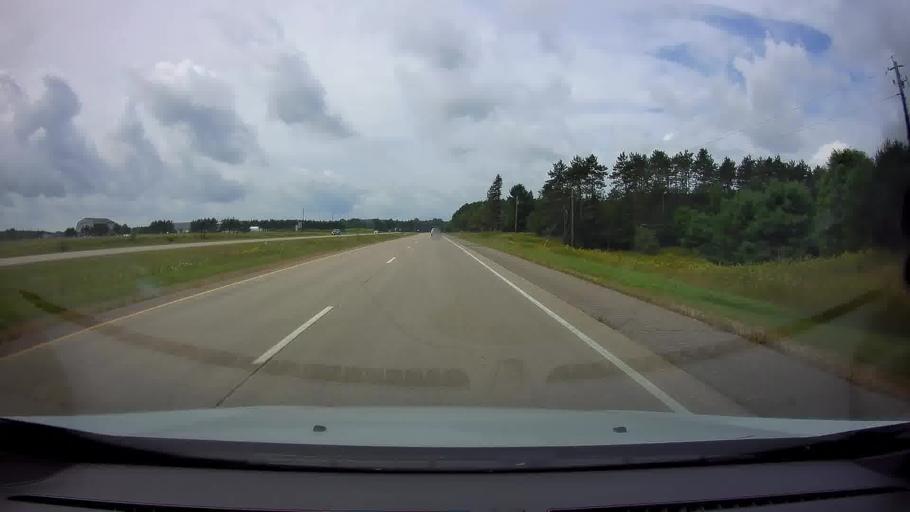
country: US
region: Wisconsin
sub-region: Shawano County
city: Wittenberg
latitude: 44.8039
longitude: -89.0228
